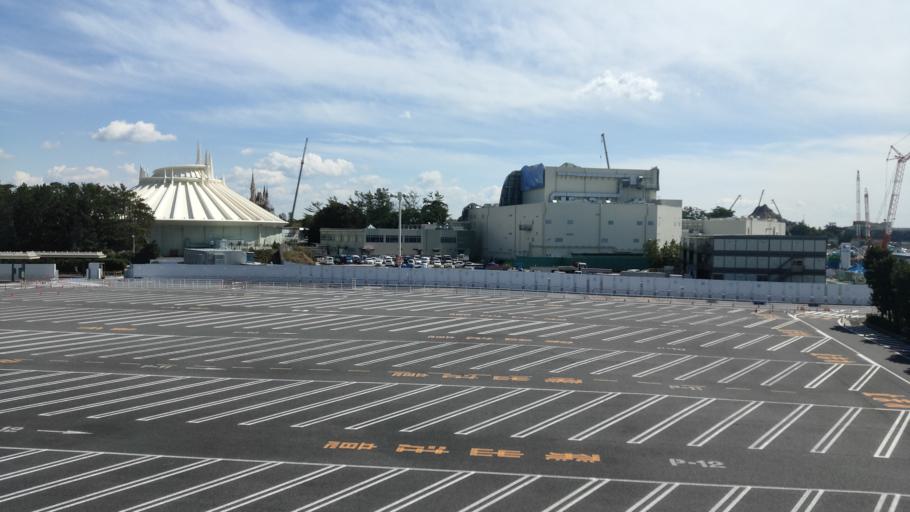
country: JP
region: Tokyo
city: Urayasu
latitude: 35.6322
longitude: 139.8750
